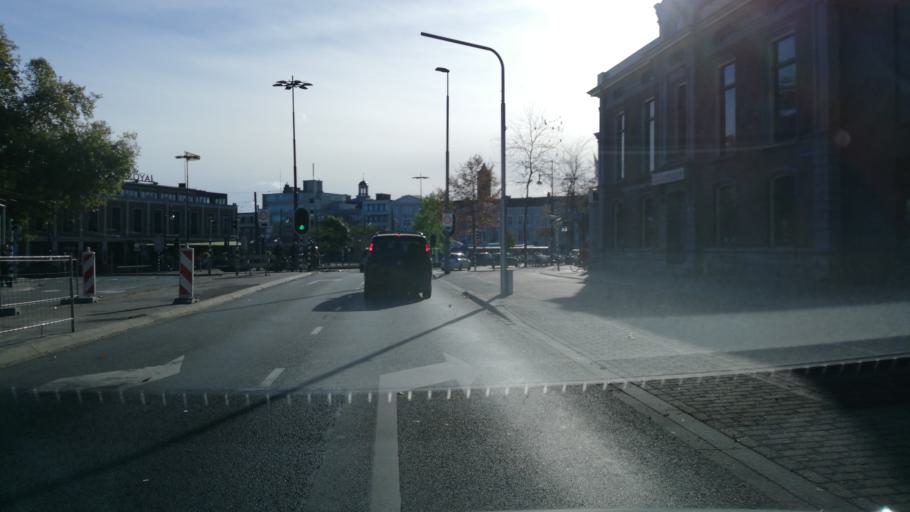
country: NL
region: Gelderland
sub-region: Gemeente Arnhem
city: Arnhem
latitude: 51.9846
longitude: 5.9053
